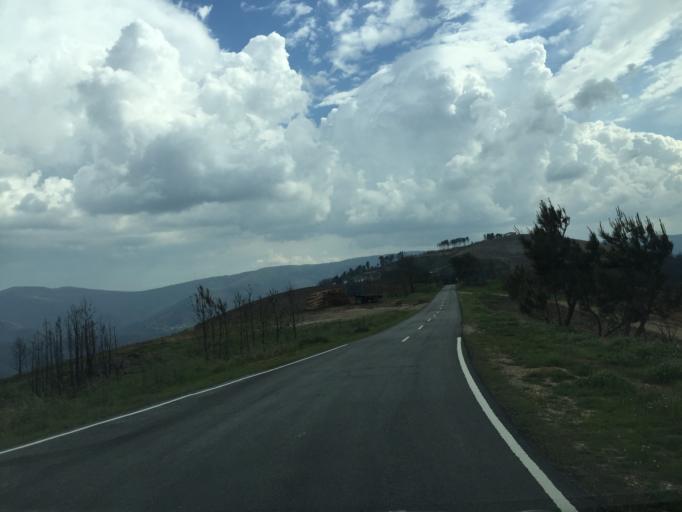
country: PT
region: Coimbra
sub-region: Arganil
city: Arganil
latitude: 40.1712
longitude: -7.9712
